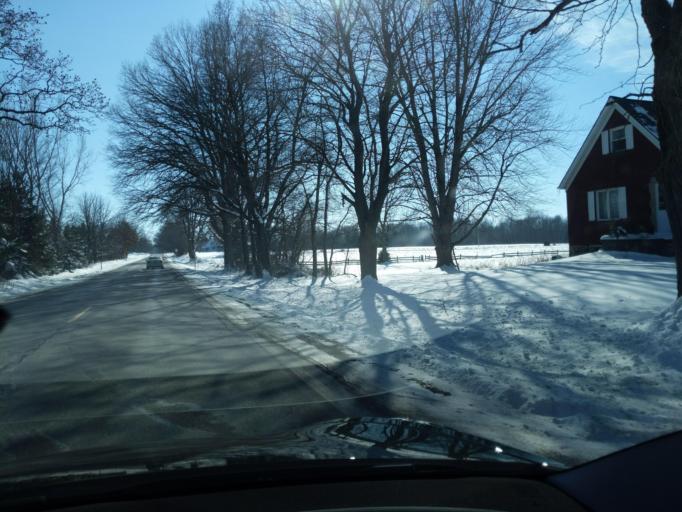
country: US
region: Michigan
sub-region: Livingston County
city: Fowlerville
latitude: 42.5370
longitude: -84.0683
